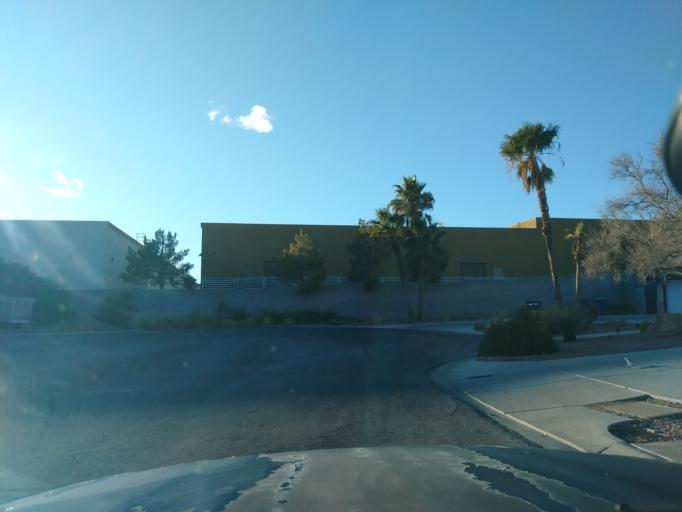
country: US
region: Nevada
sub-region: Clark County
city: Spring Valley
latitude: 36.1492
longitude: -115.2416
